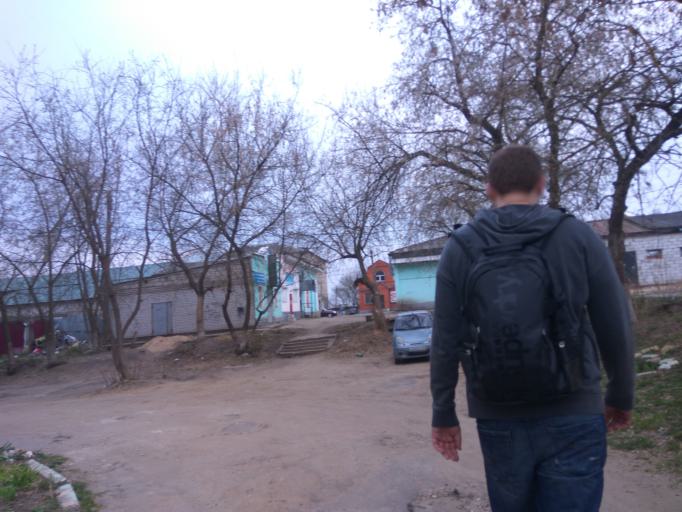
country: RU
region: Vladimir
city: Aleksandrov
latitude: 56.3983
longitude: 38.7298
